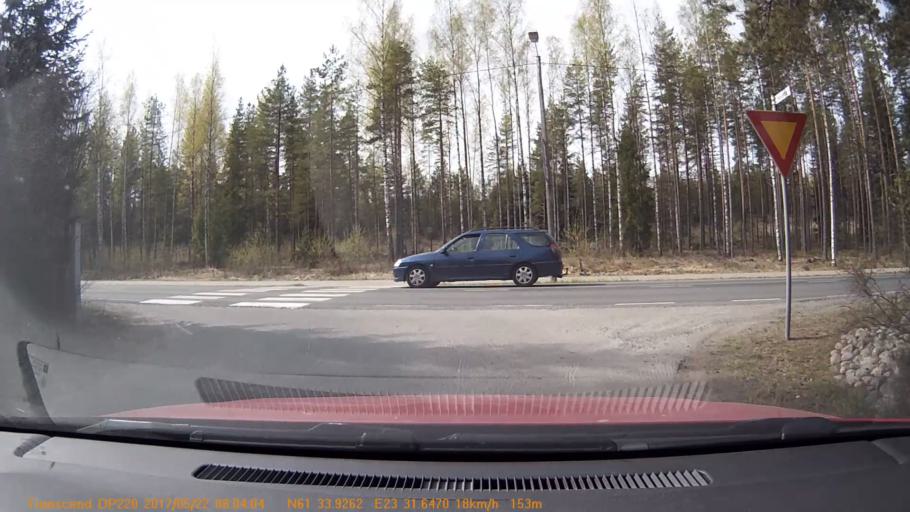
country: FI
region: Pirkanmaa
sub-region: Tampere
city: Yloejaervi
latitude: 61.5655
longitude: 23.5275
